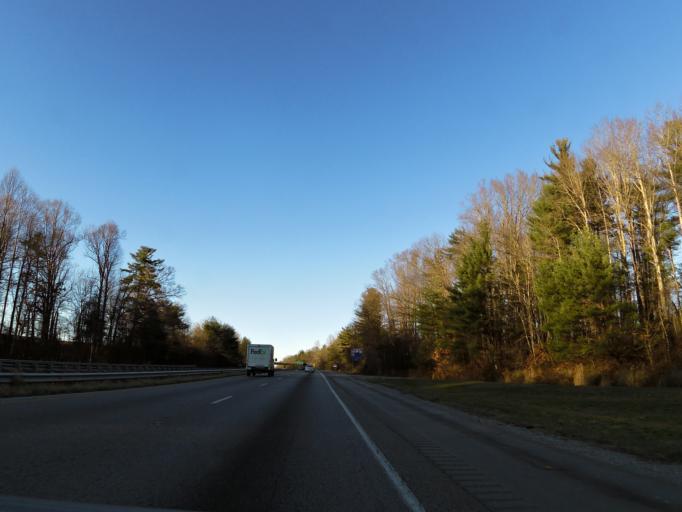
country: US
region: North Carolina
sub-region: Henderson County
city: East Flat Rock
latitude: 35.2868
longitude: -82.4009
